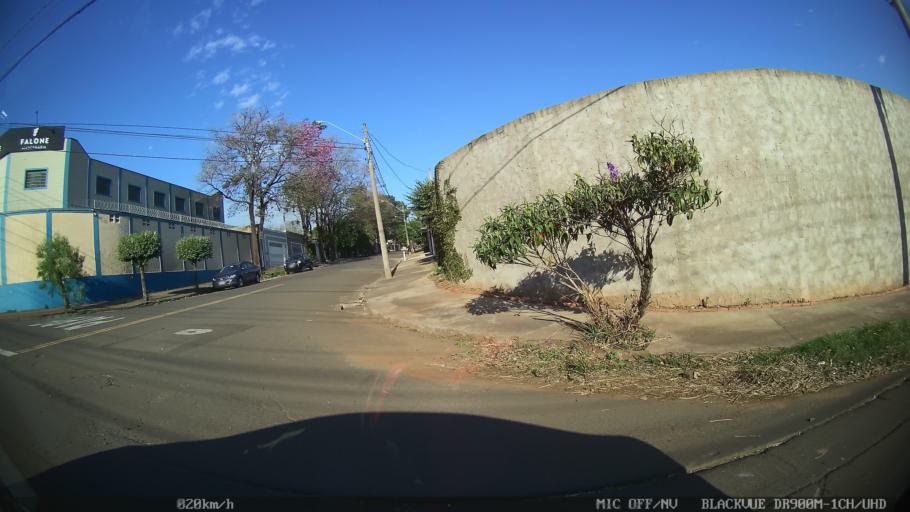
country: BR
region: Sao Paulo
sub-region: Piracicaba
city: Piracicaba
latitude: -22.6741
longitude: -47.6299
